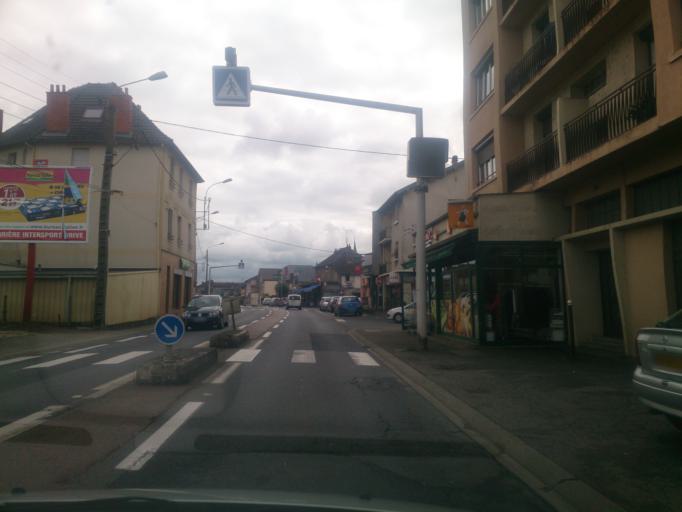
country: FR
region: Limousin
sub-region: Departement de la Correze
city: Brive-la-Gaillarde
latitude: 45.1647
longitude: 1.5168
